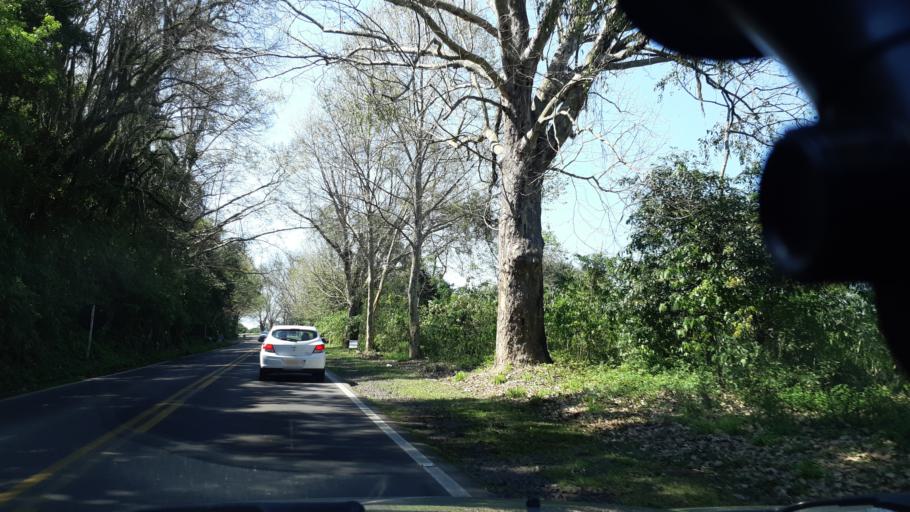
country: BR
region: Rio Grande do Sul
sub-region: Nova Petropolis
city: Nova Petropolis
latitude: -29.4049
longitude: -51.1279
